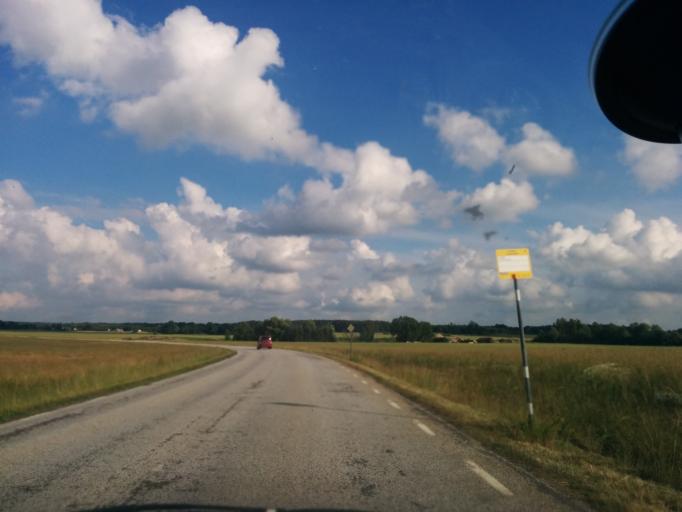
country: SE
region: Skane
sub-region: Lunds Kommun
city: Genarp
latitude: 55.6074
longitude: 13.3681
